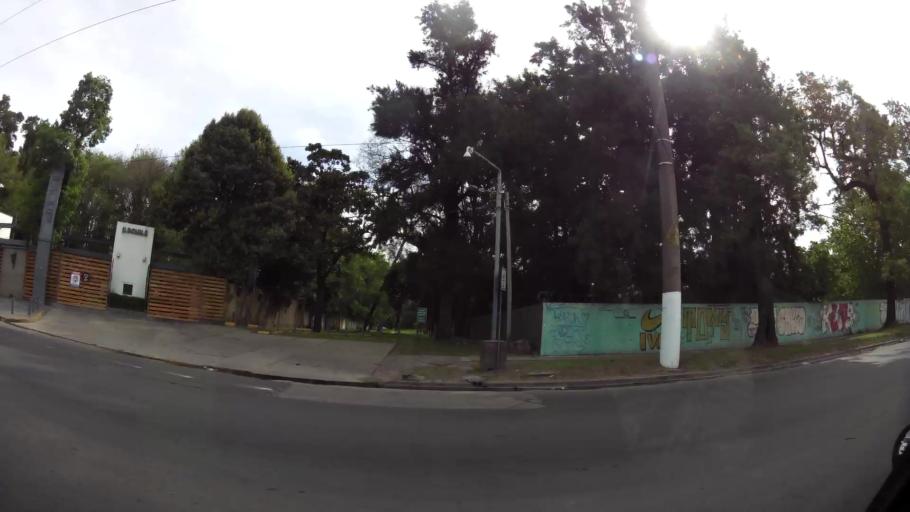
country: AR
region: Buenos Aires
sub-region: Partido de Quilmes
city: Quilmes
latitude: -34.7493
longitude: -58.2689
